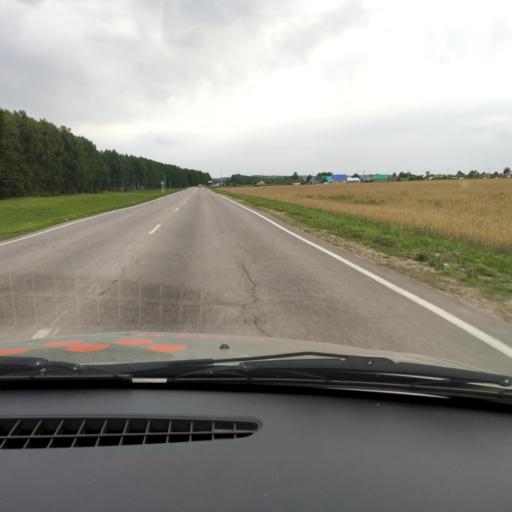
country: RU
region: Bashkortostan
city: Krasnaya Gorka
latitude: 55.1010
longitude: 56.6255
